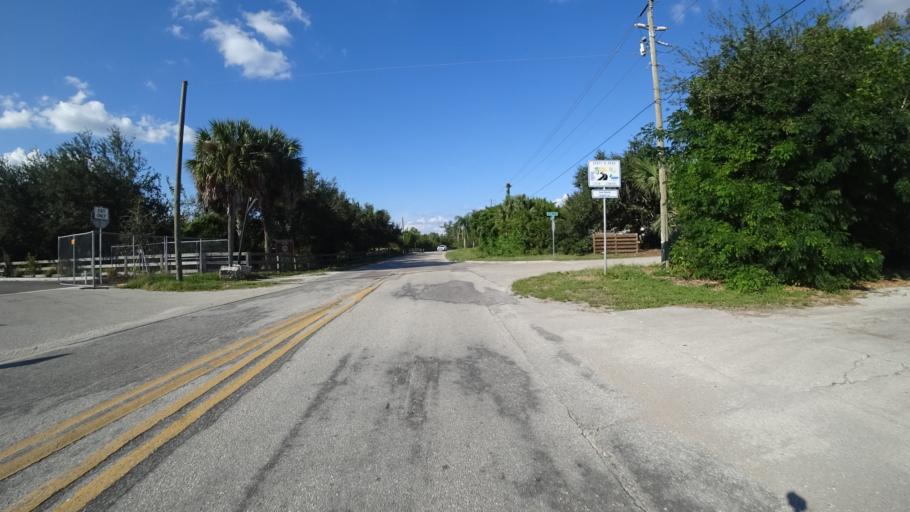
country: US
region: Florida
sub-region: Manatee County
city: Cortez
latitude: 27.4626
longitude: -82.6485
